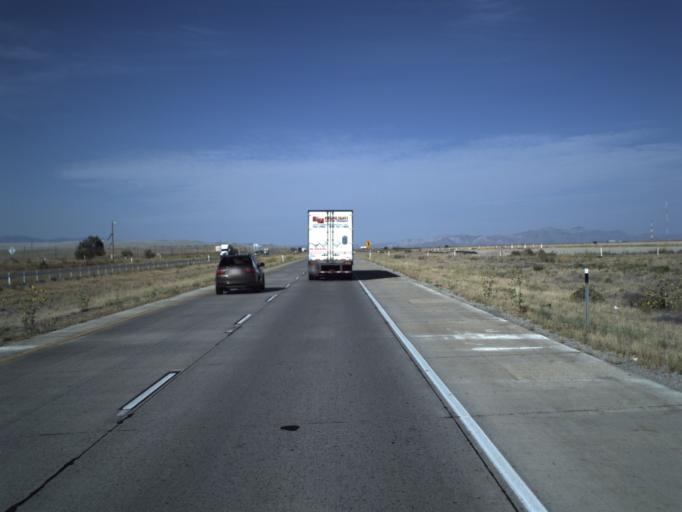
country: US
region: Utah
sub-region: Salt Lake County
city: Magna
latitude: 40.7711
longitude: -112.0650
